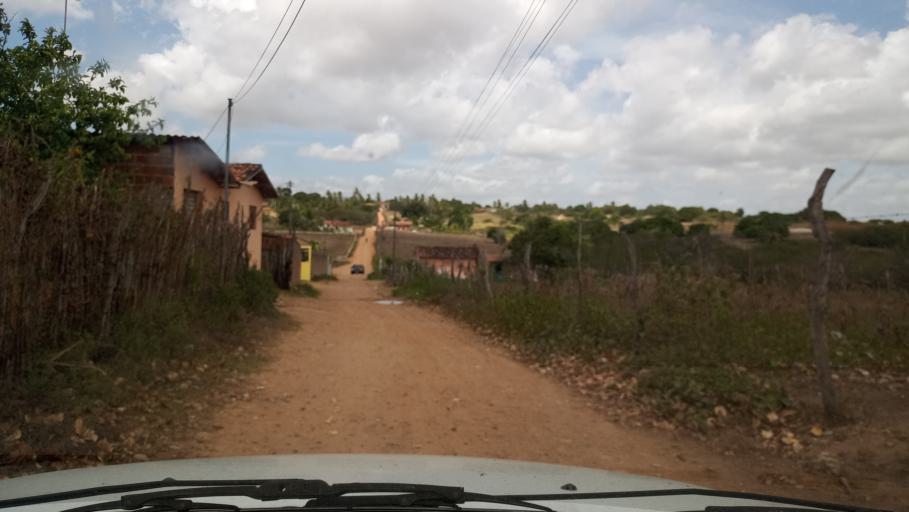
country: BR
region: Rio Grande do Norte
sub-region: Goianinha
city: Goianinha
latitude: -6.2985
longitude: -35.2771
